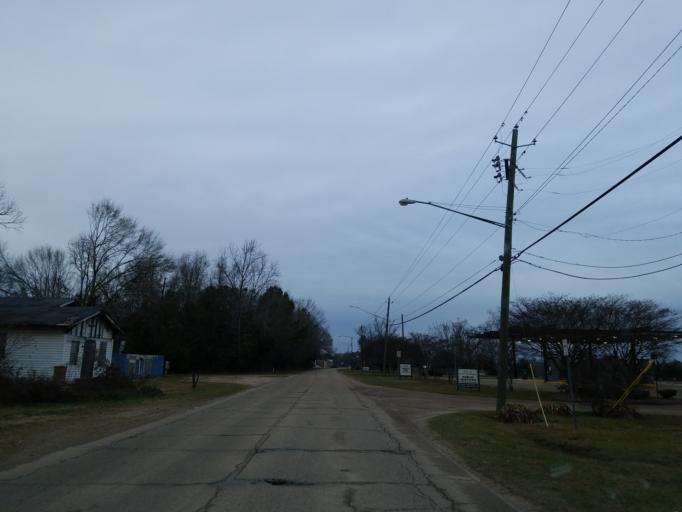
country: US
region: Mississippi
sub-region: Forrest County
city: Hattiesburg
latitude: 31.3083
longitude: -89.2796
